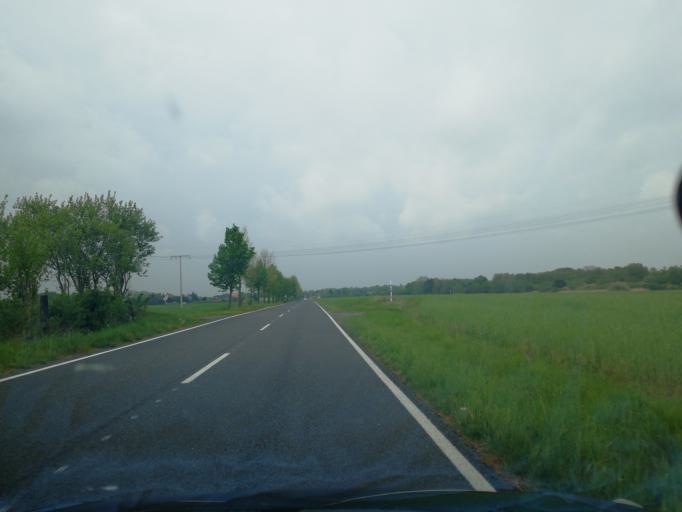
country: DE
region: Brandenburg
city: Calau
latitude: 51.7509
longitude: 13.9788
